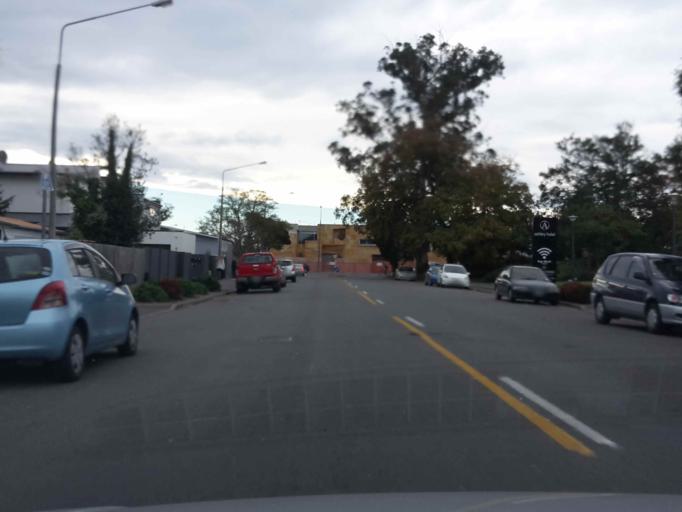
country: NZ
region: Canterbury
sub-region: Christchurch City
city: Christchurch
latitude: -43.5304
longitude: 172.6062
